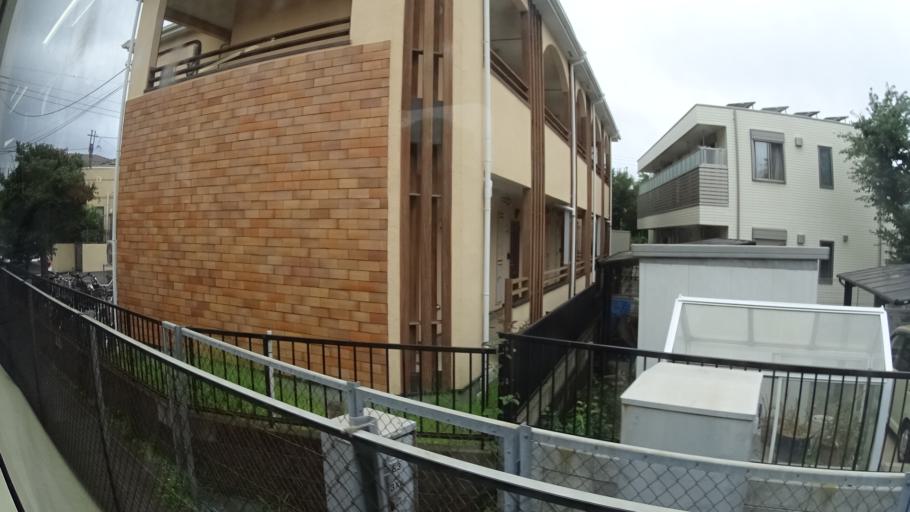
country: JP
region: Kanagawa
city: Fujisawa
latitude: 35.3280
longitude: 139.4851
